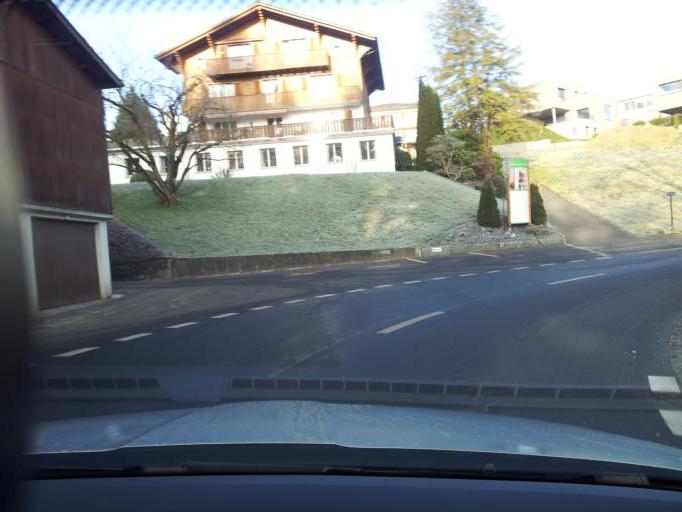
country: CH
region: Lucerne
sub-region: Sursee District
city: Neuenkirch
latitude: 47.0692
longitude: 8.2000
